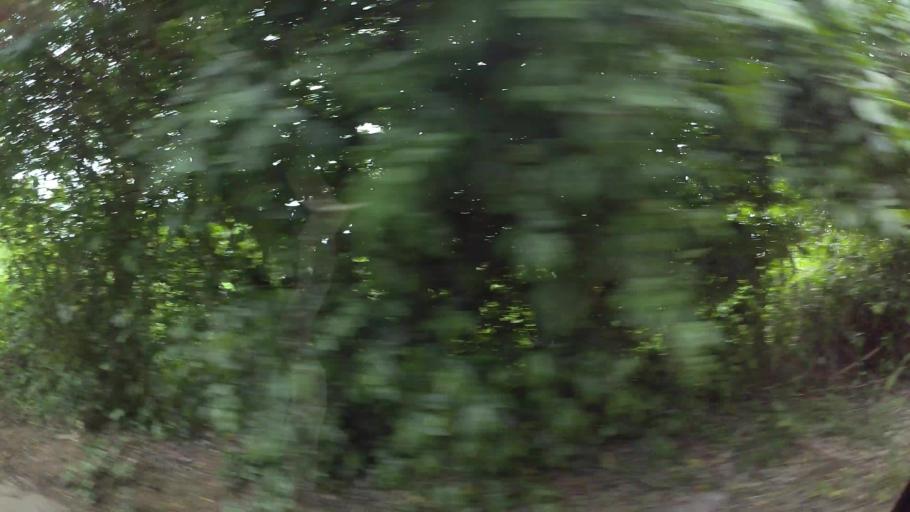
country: TH
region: Chon Buri
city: Sattahip
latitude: 12.7114
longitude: 100.8985
